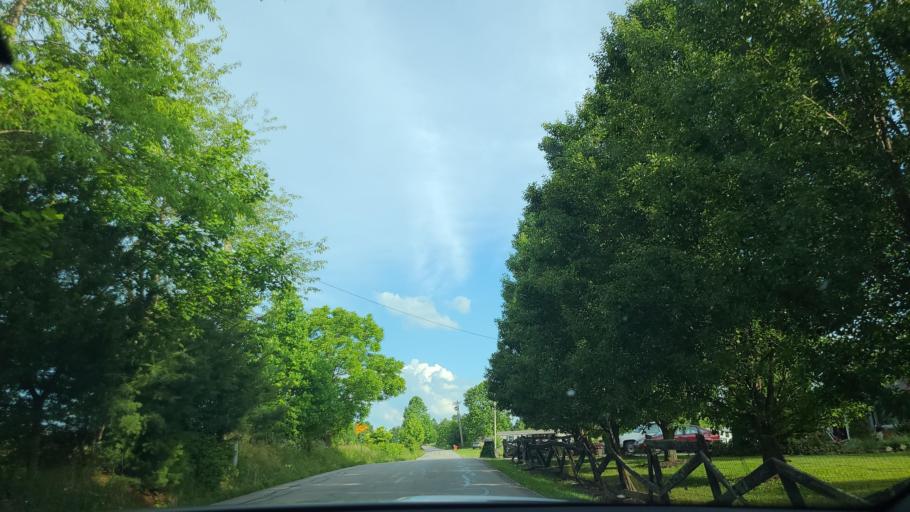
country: US
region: Kentucky
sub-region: Whitley County
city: Corbin
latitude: 36.9007
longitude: -84.2357
